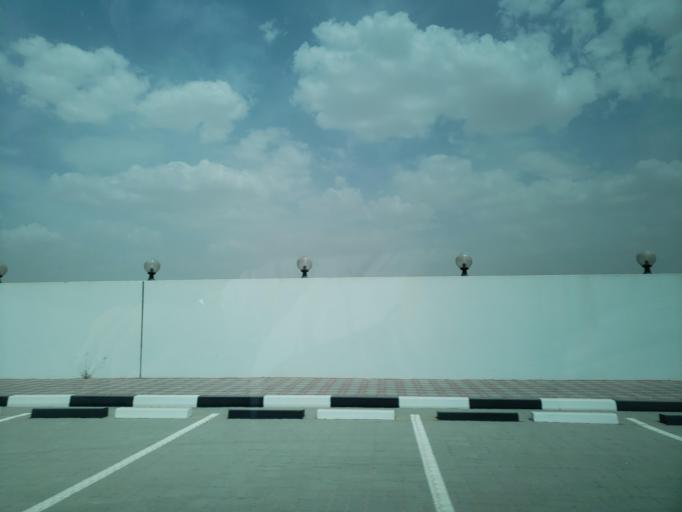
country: AE
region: Ash Shariqah
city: Sharjah
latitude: 25.3080
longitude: 55.5846
